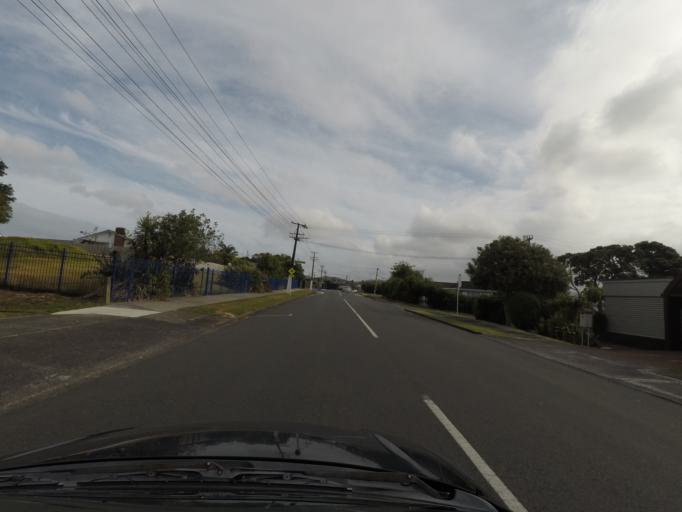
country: NZ
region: Auckland
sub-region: Auckland
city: Waitakere
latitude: -36.9053
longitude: 174.6641
